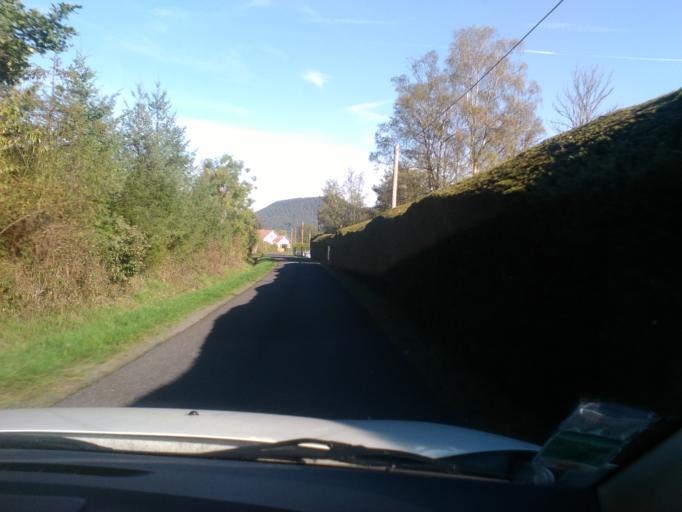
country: FR
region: Lorraine
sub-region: Departement des Vosges
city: Taintrux
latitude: 48.2345
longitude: 6.8833
